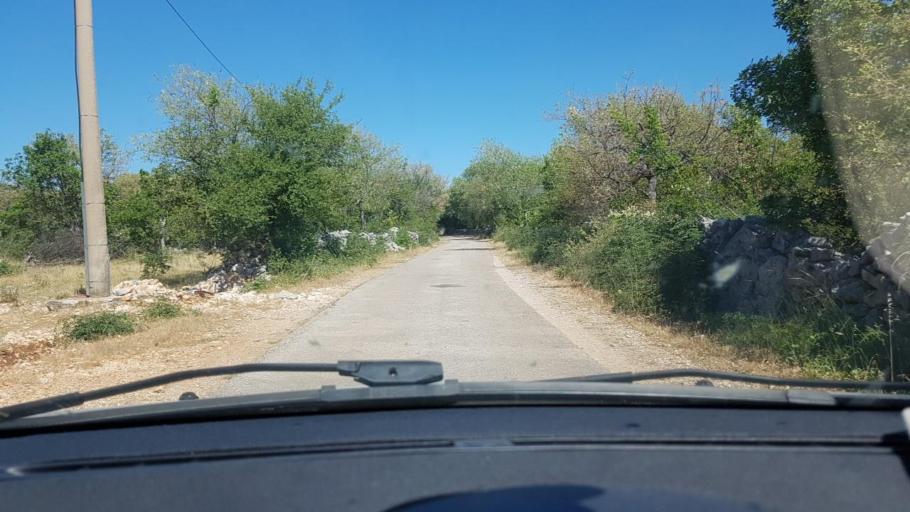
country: HR
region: Sibensko-Kniniska
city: Kistanje
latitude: 44.0373
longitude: 16.0579
